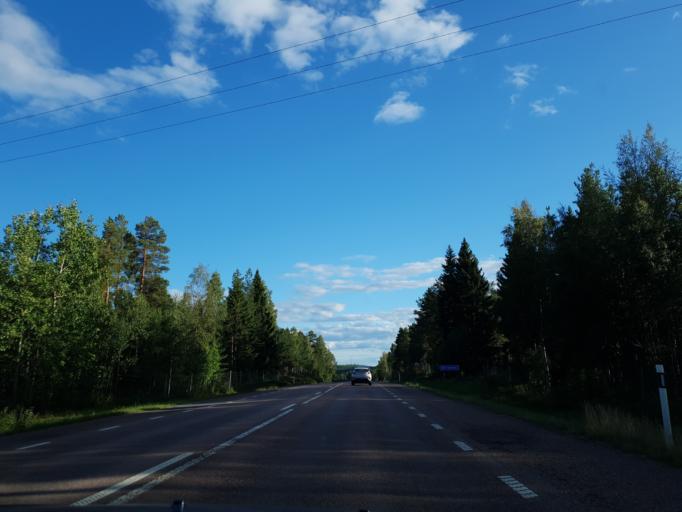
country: SE
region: Gaevleborg
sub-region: Nordanstigs Kommun
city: Bergsjoe
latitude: 61.9821
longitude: 17.2411
